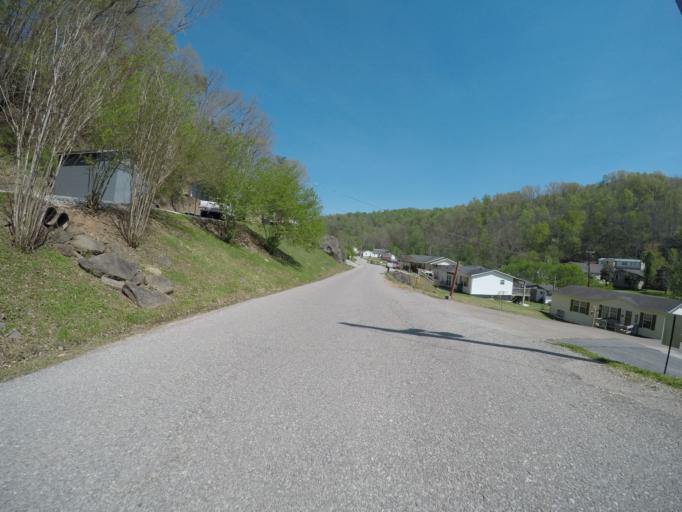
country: US
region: West Virginia
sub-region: Kanawha County
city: Charleston
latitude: 38.4139
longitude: -81.6115
